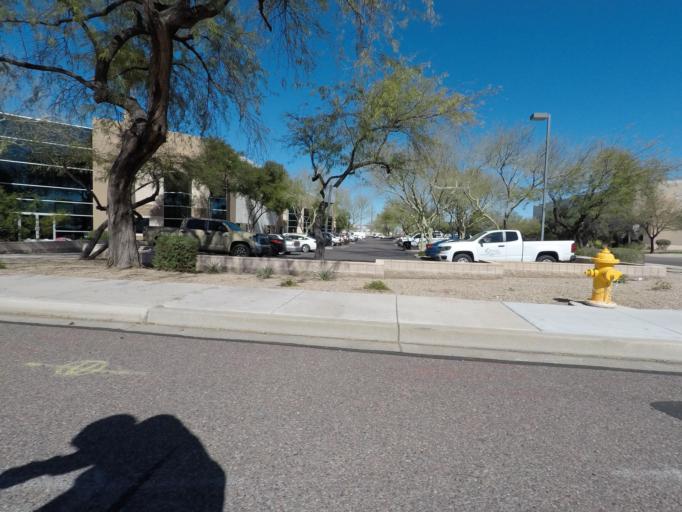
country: US
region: Arizona
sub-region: Maricopa County
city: Tempe Junction
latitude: 33.4151
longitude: -111.9870
